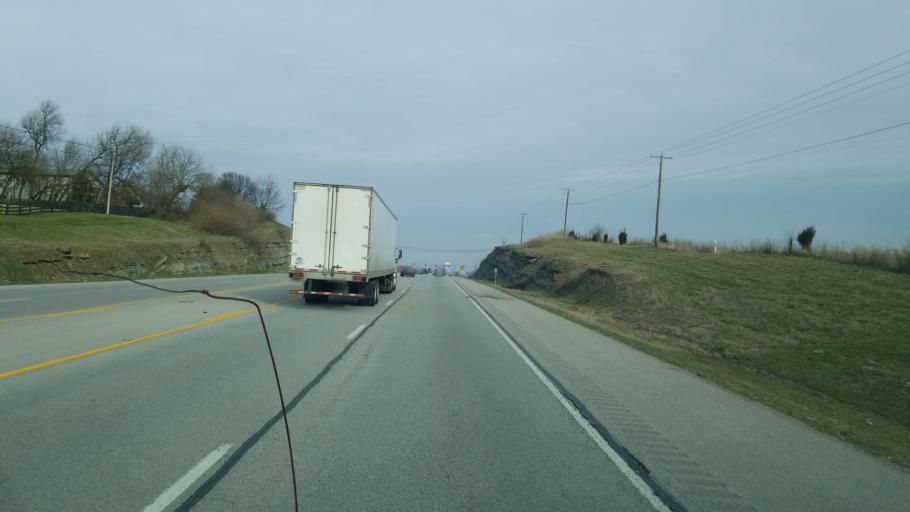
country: US
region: Kentucky
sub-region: Boyle County
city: Junction City
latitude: 37.6102
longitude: -84.7741
